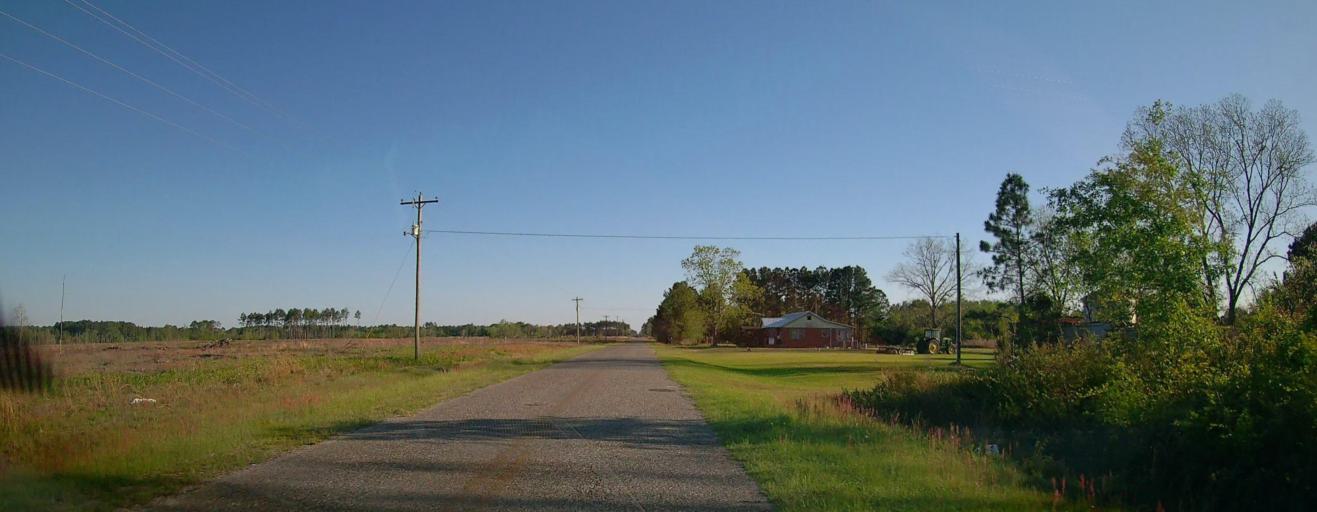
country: US
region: Georgia
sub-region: Ben Hill County
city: Fitzgerald
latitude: 31.6820
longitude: -83.1466
